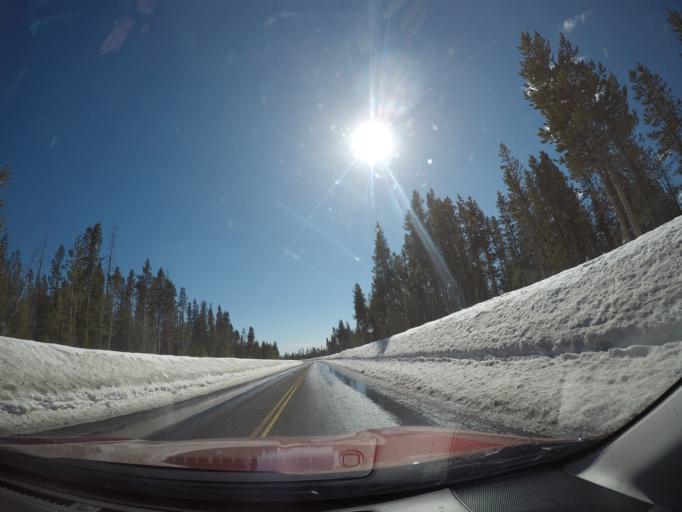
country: US
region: Oregon
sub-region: Deschutes County
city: Sunriver
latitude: 43.9674
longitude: -121.6175
